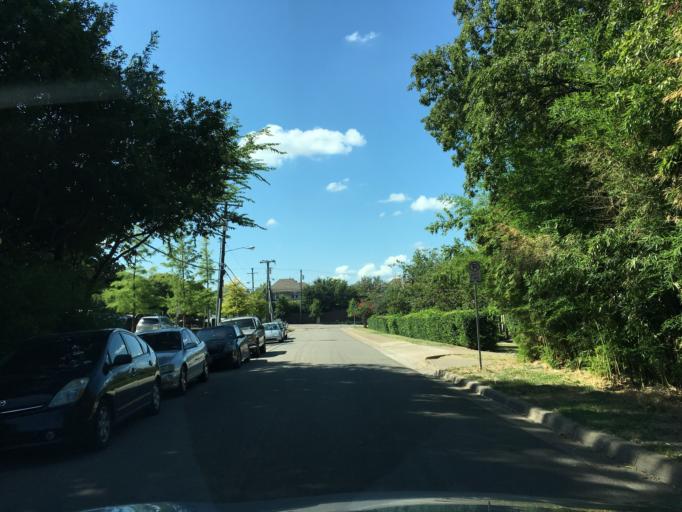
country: US
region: Texas
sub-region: Dallas County
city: Garland
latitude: 32.8655
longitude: -96.6973
